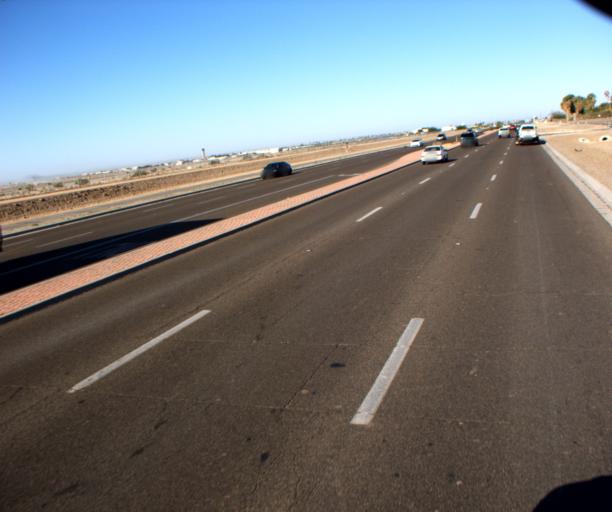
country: US
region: Arizona
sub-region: Yuma County
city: Yuma
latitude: 32.6696
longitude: -114.5904
